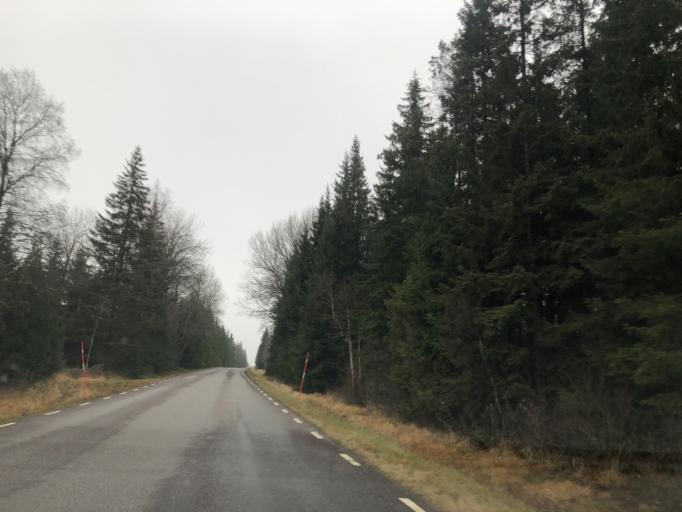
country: SE
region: Vaestra Goetaland
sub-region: Ulricehamns Kommun
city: Ulricehamn
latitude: 57.7275
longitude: 13.5475
